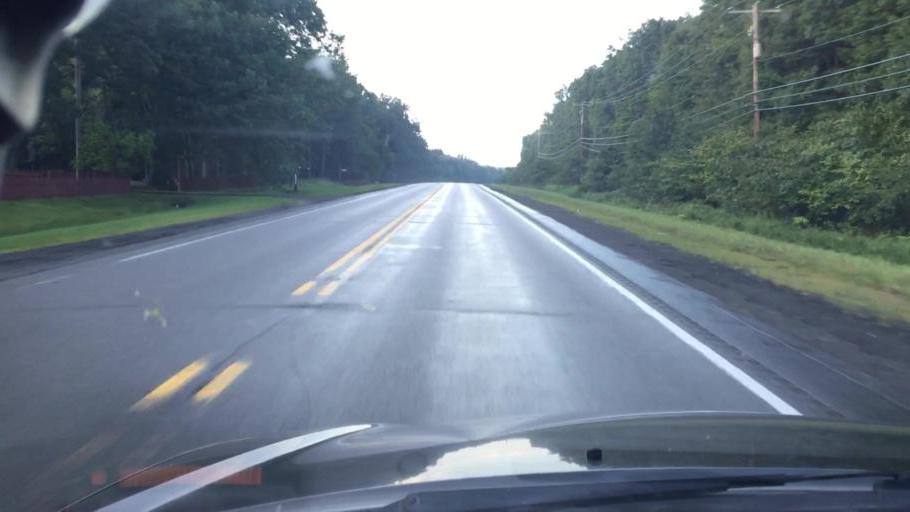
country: US
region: Pennsylvania
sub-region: Carbon County
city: Jim Thorpe
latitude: 40.9200
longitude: -75.6668
